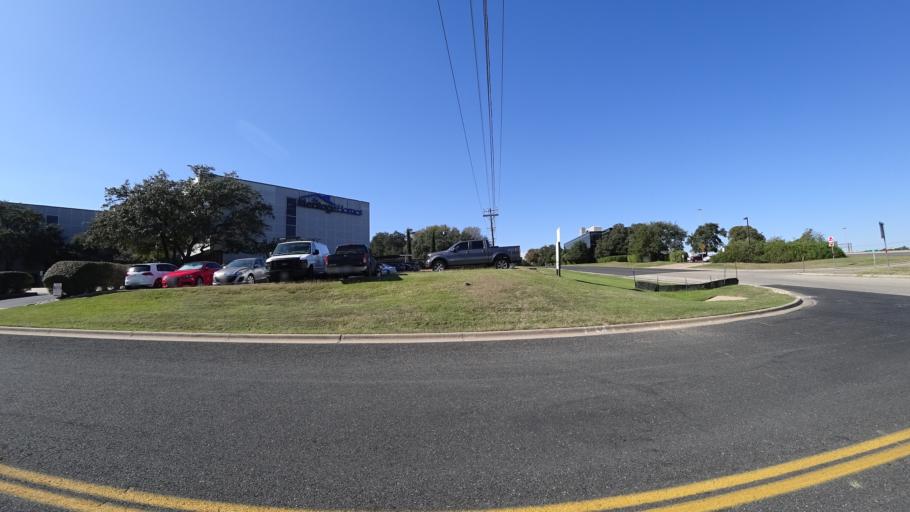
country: US
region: Texas
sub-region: Williamson County
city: Jollyville
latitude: 30.3800
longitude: -97.7410
